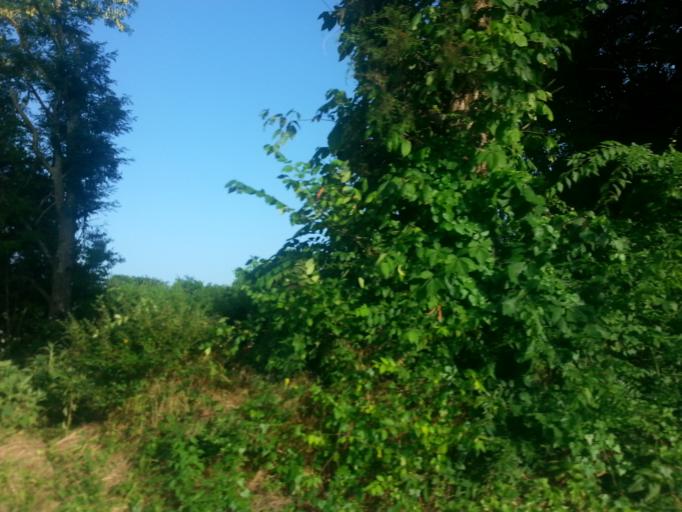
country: US
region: Tennessee
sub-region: Loudon County
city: Greenback
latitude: 35.7414
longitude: -84.1660
